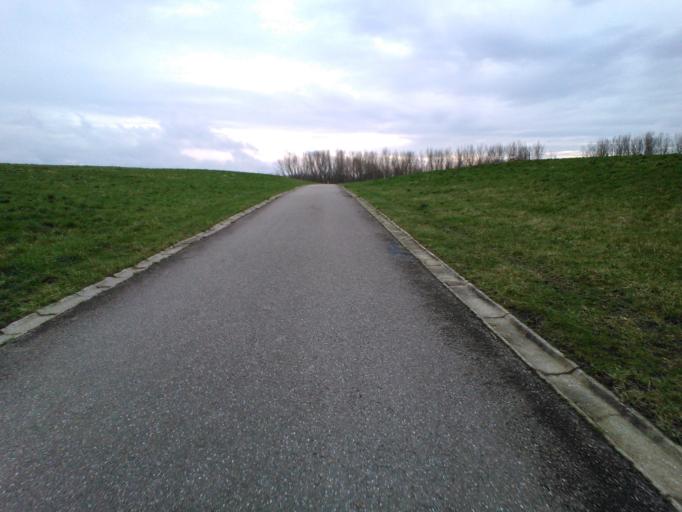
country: NL
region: South Holland
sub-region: Gemeente Lansingerland
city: Bleiswijk
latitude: 51.9781
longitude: 4.5414
